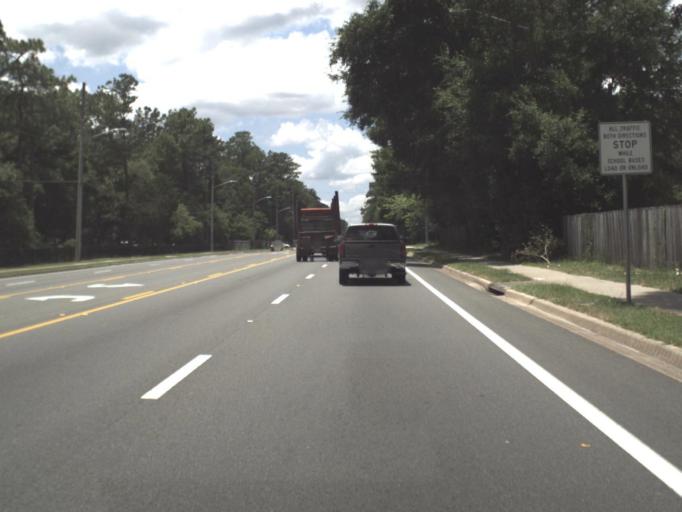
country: US
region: Florida
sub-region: Alachua County
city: Gainesville
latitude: 29.6886
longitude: -82.3487
